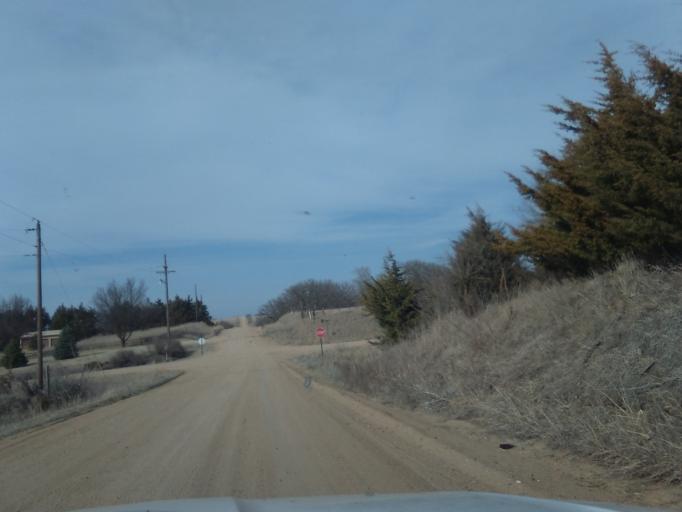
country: US
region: Nebraska
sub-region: Jefferson County
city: Fairbury
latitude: 40.2184
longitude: -97.2364
